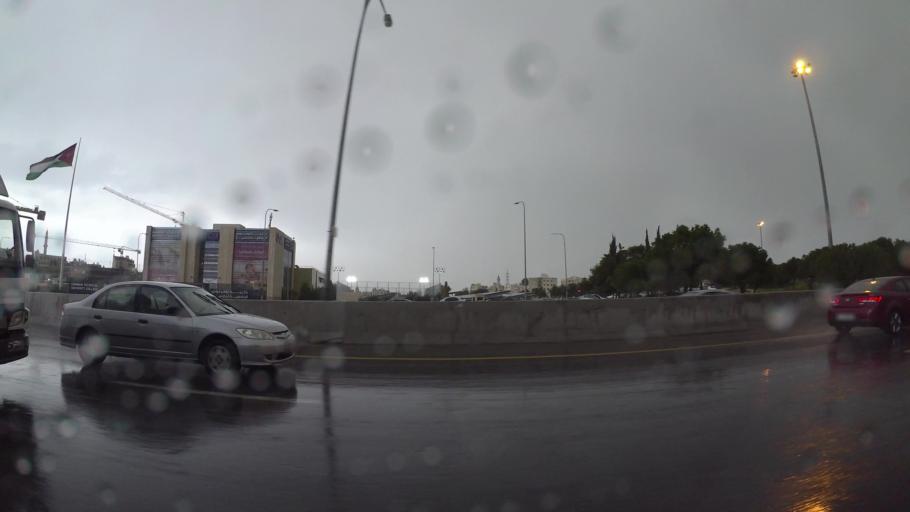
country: JO
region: Amman
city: Umm as Summaq
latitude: 31.8988
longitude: 35.8698
